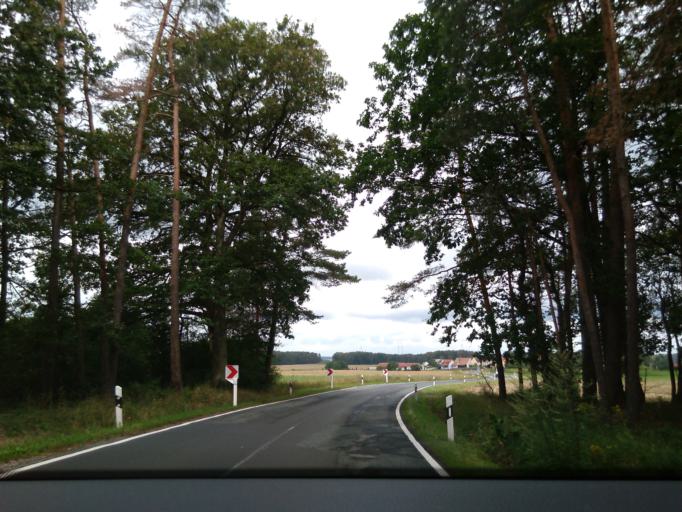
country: DE
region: Bavaria
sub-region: Regierungsbezirk Mittelfranken
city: Gremsdorf
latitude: 49.6628
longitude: 10.8068
